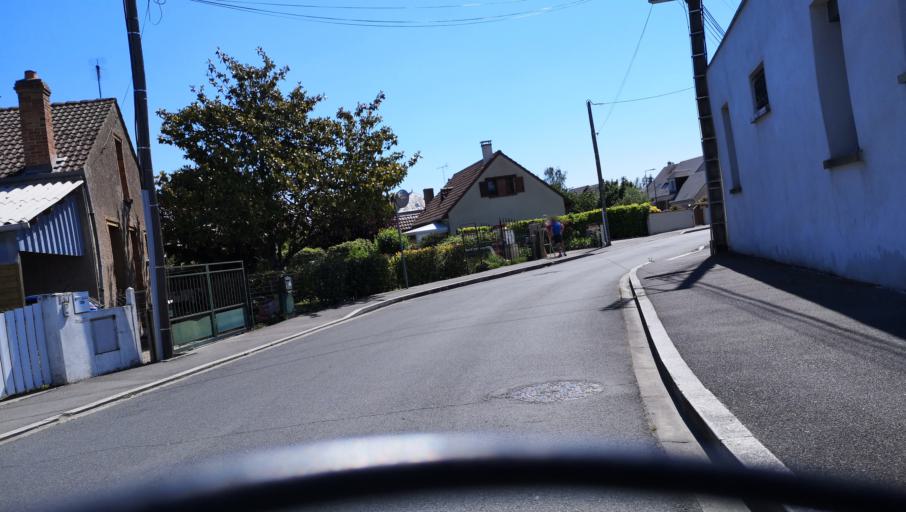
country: FR
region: Centre
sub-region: Departement du Loiret
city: Saint-Pryve-Saint-Mesmin
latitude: 47.8850
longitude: 1.8866
